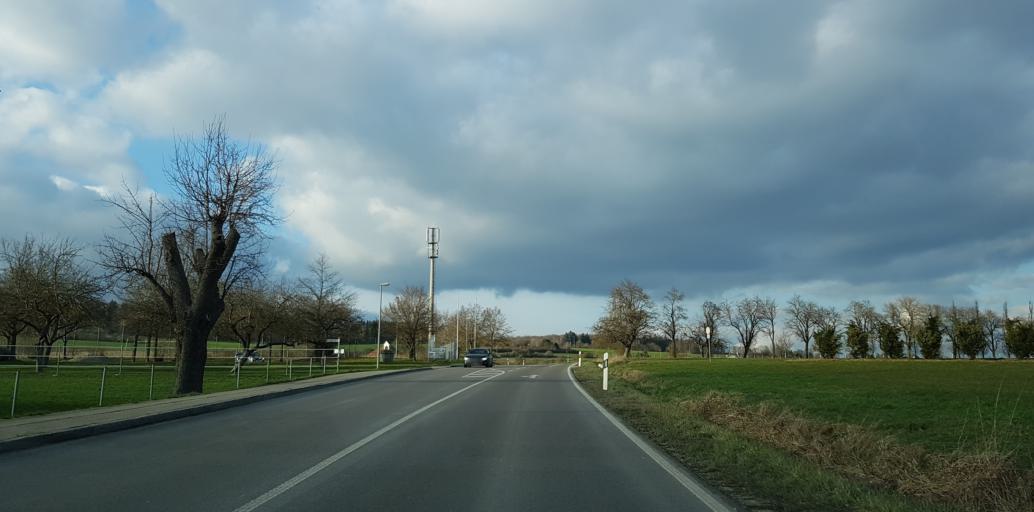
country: DE
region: Baden-Wuerttemberg
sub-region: Tuebingen Region
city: Erbach
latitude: 48.3672
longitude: 9.8795
